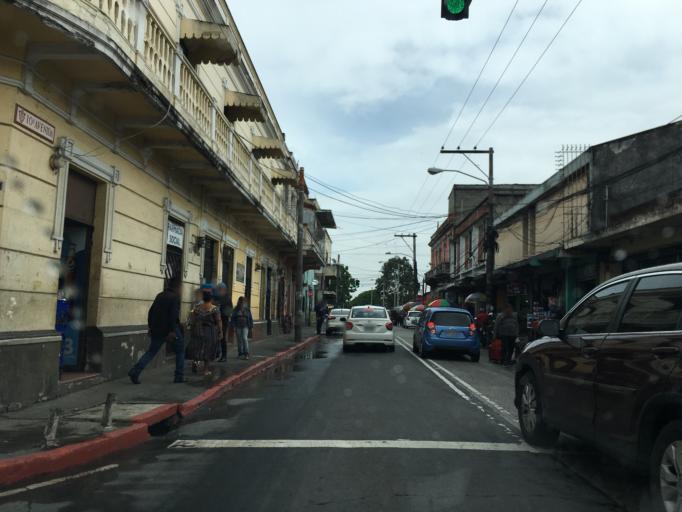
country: GT
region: Guatemala
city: Guatemala City
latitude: 14.6311
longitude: -90.5109
